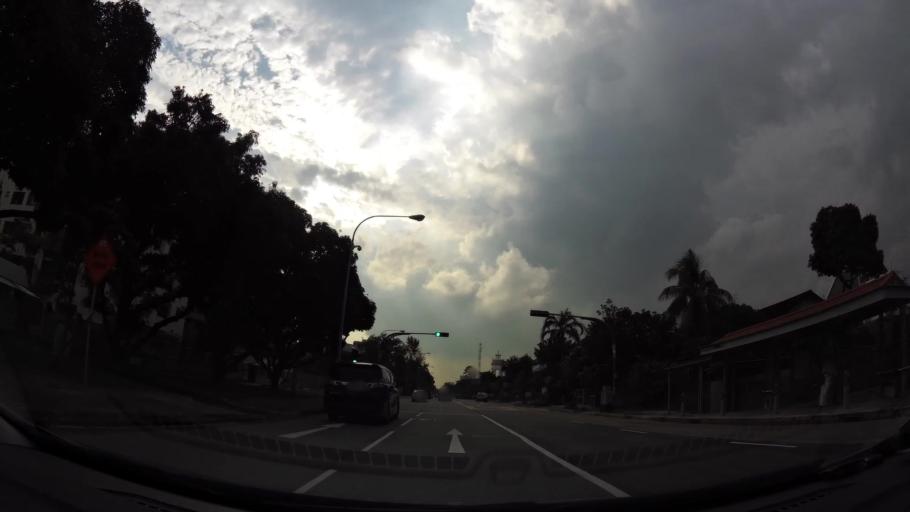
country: SG
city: Singapore
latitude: 1.3146
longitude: 103.9383
